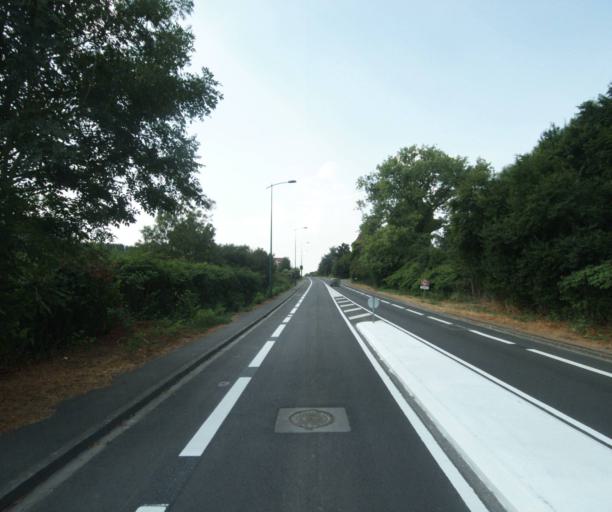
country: FR
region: Nord-Pas-de-Calais
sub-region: Departement du Nord
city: Bondues
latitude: 50.7248
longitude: 3.1002
